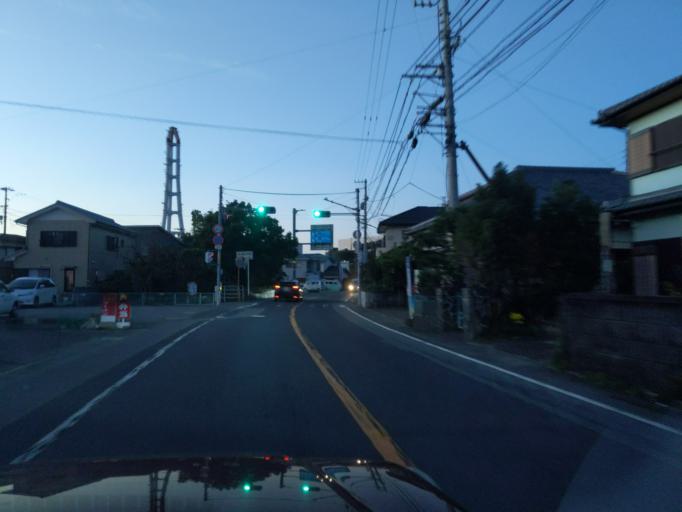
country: JP
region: Tokushima
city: Anan
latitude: 33.8846
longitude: 134.6529
